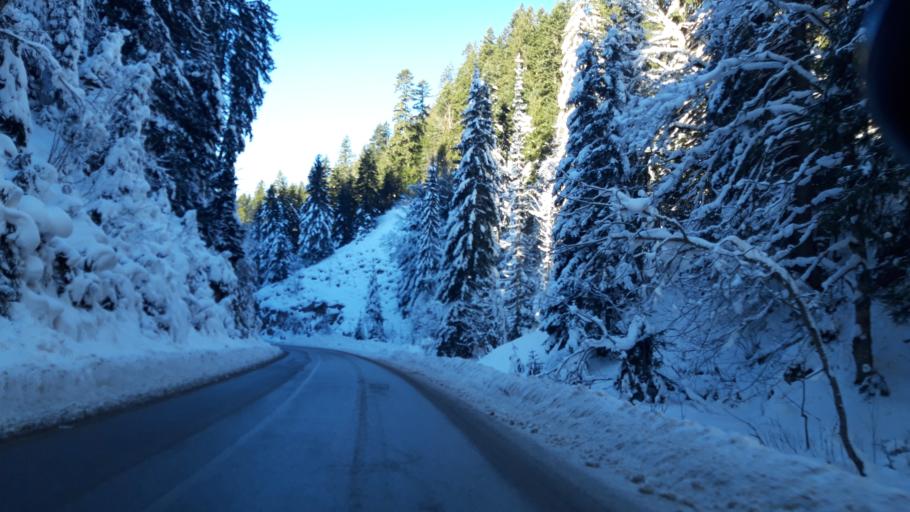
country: BA
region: Republika Srpska
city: Koran
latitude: 43.7473
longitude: 18.5649
